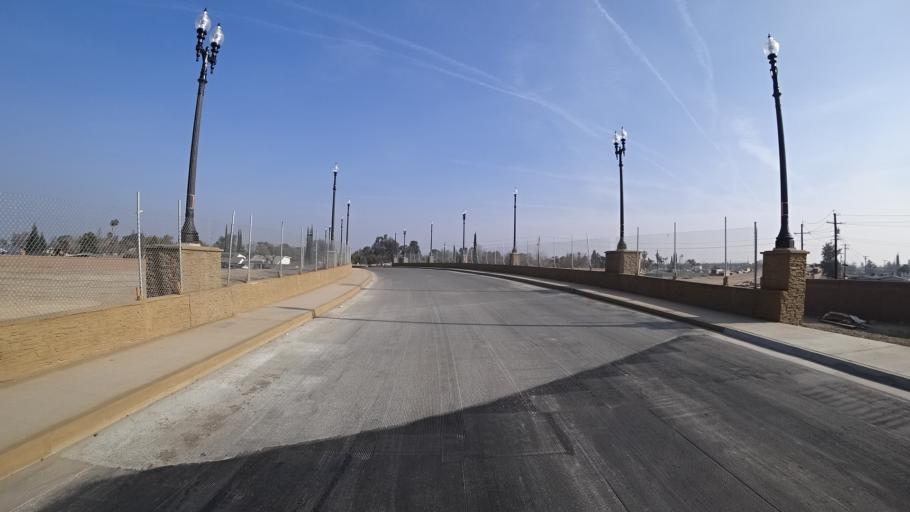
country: US
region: California
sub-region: Kern County
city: Bakersfield
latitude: 35.3585
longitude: -119.0513
